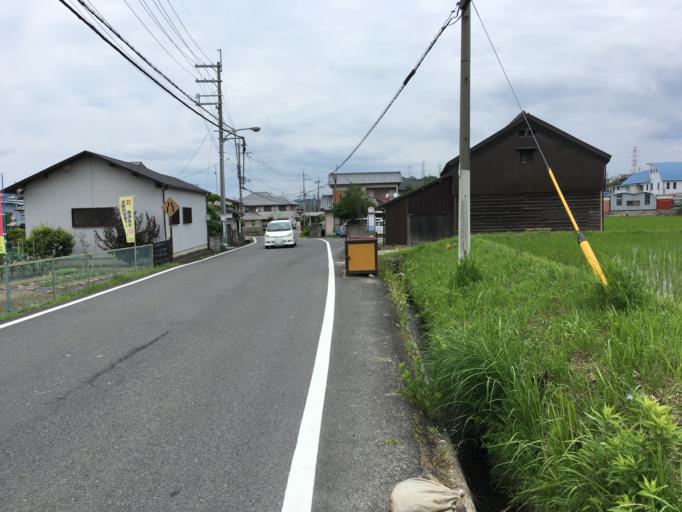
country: JP
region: Nara
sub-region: Ikoma-shi
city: Ikoma
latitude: 34.7215
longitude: 135.7047
